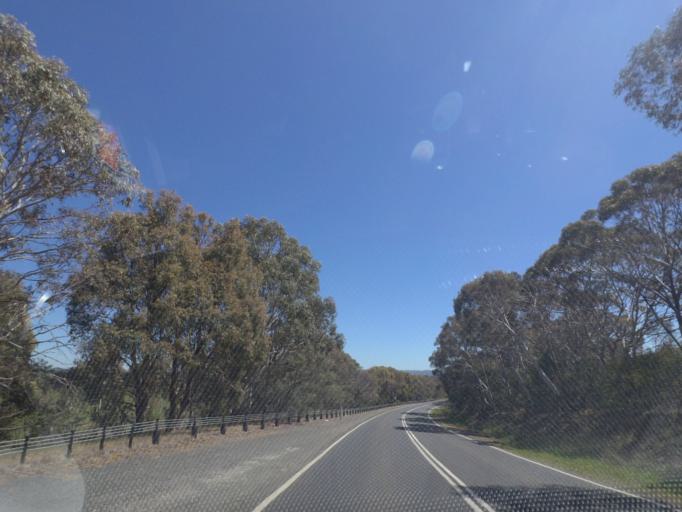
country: AU
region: Victoria
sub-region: Hume
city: Sunbury
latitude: -37.2906
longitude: 144.7904
